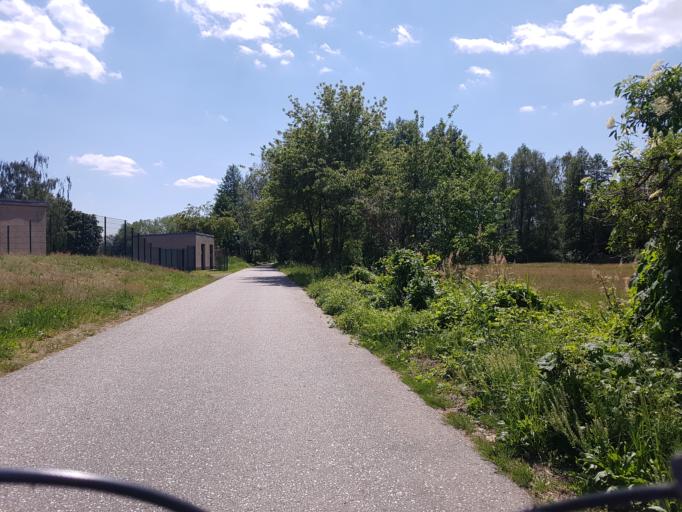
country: DE
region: Brandenburg
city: Bad Liebenwerda
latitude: 51.5440
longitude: 13.3651
